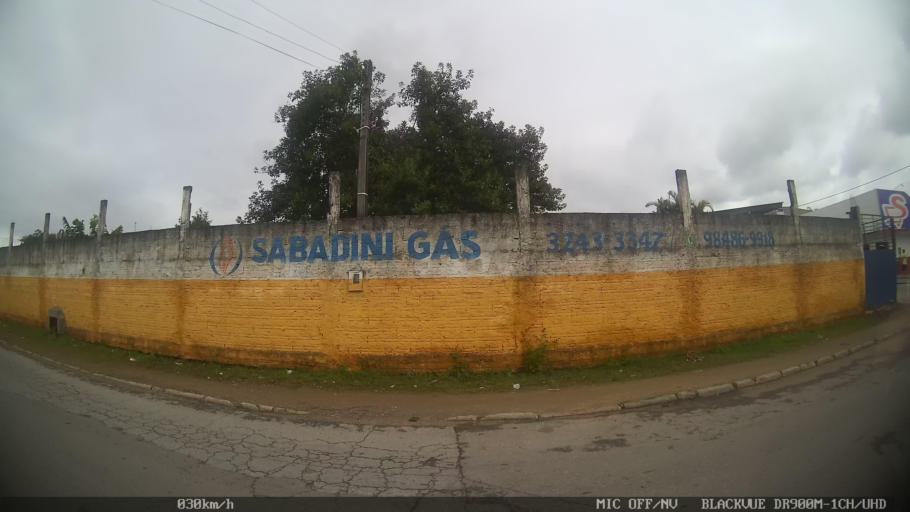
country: BR
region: Santa Catarina
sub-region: Biguacu
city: Biguacu
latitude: -27.5128
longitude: -48.6429
